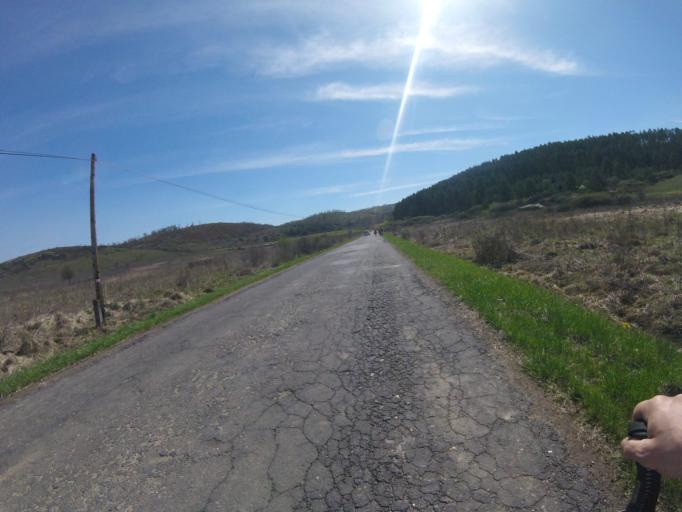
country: HU
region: Borsod-Abauj-Zemplen
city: Szendro
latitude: 48.4104
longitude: 20.7431
